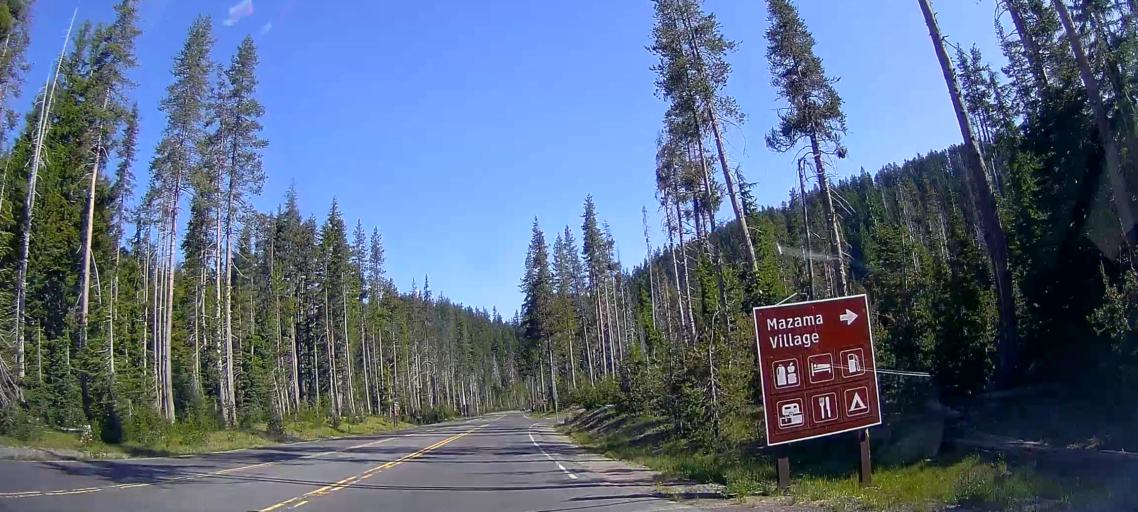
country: US
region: Oregon
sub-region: Jackson County
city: Shady Cove
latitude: 42.8691
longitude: -122.1692
